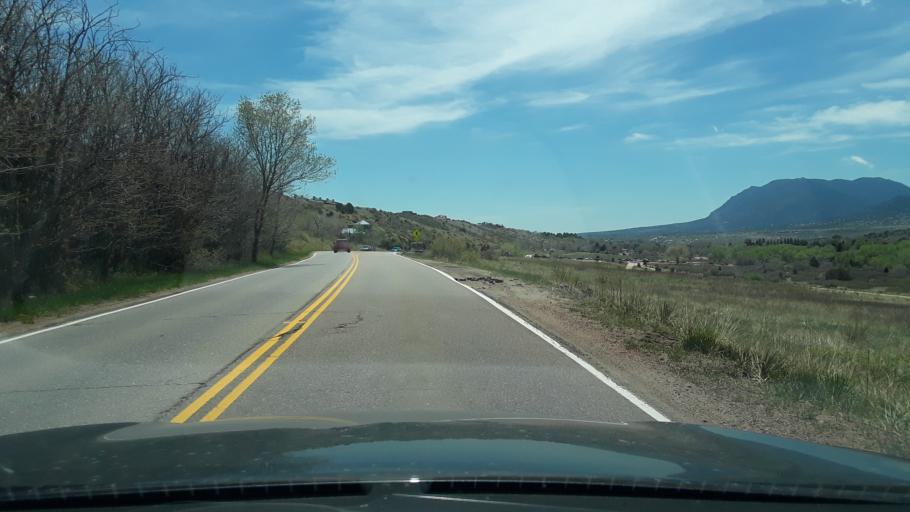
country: US
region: Colorado
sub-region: El Paso County
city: Manitou Springs
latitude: 38.8817
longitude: -104.8727
